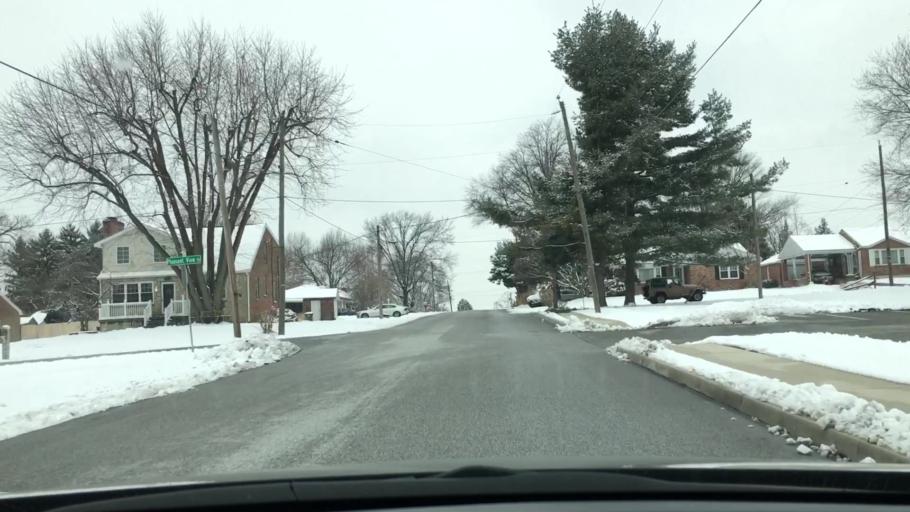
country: US
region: Pennsylvania
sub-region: York County
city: North York
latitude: 39.9970
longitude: -76.7079
